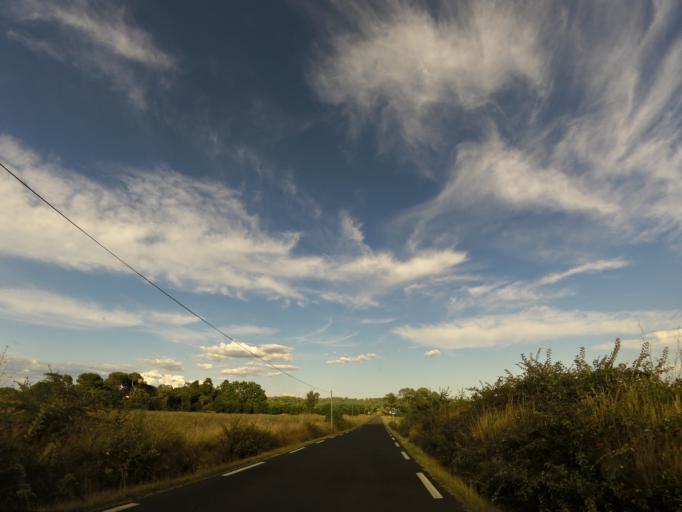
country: FR
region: Languedoc-Roussillon
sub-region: Departement de l'Herault
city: Boisseron
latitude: 43.7806
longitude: 4.0507
